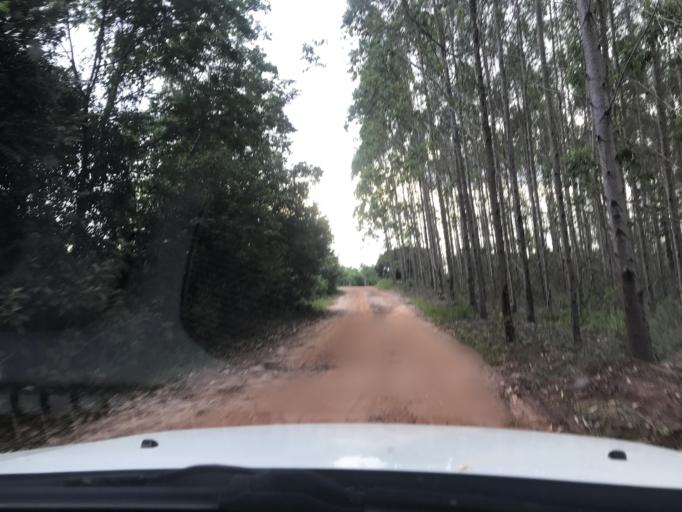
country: BR
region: Bahia
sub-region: Entre Rios
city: Entre Rios
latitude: -12.0954
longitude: -38.1945
